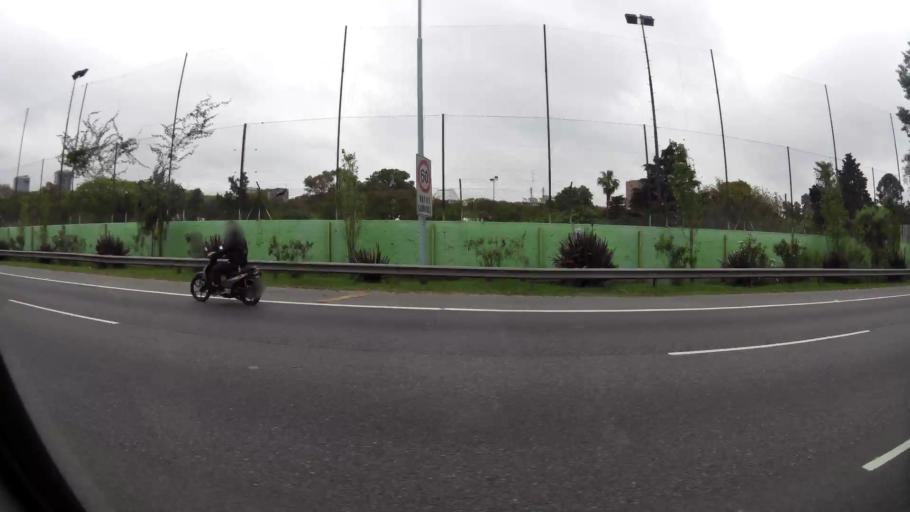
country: AR
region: Buenos Aires F.D.
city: Colegiales
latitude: -34.5465
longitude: -58.4420
